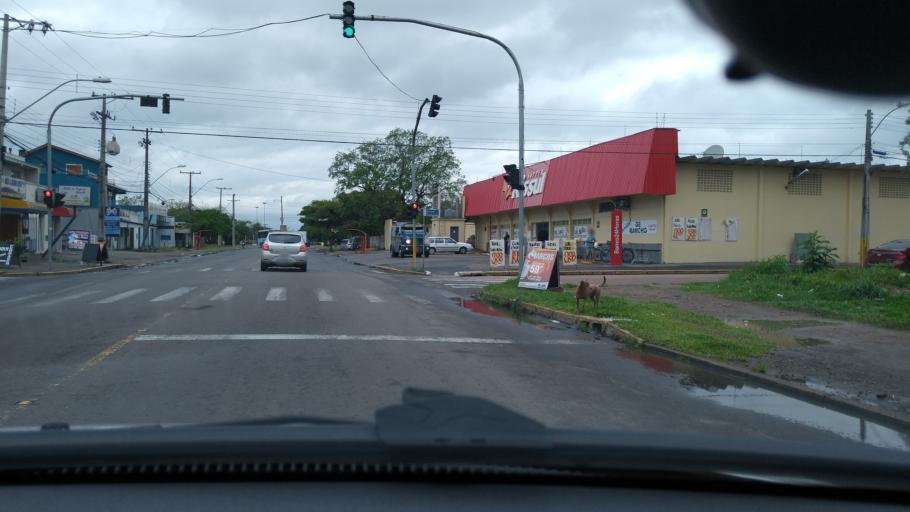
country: BR
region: Rio Grande do Sul
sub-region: Canoas
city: Canoas
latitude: -29.9019
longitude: -51.2071
